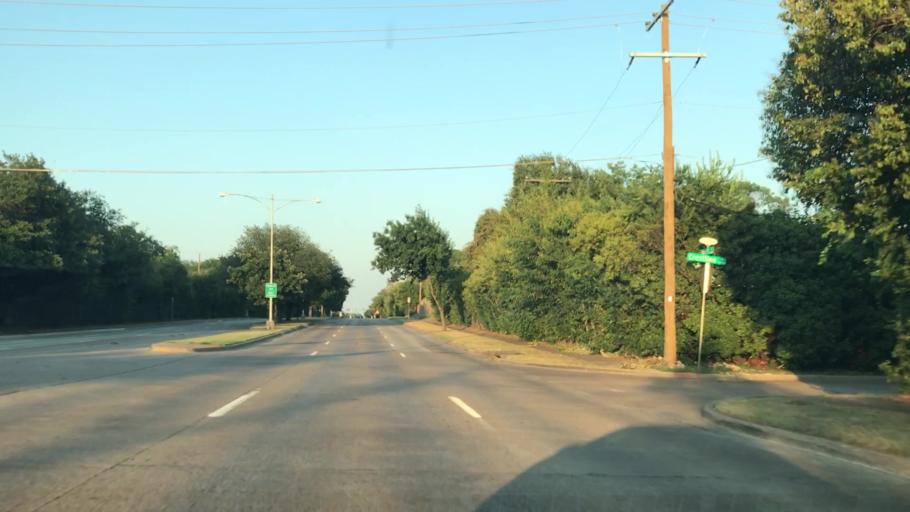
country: US
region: Texas
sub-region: Dallas County
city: Addison
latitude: 32.9095
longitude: -96.8345
